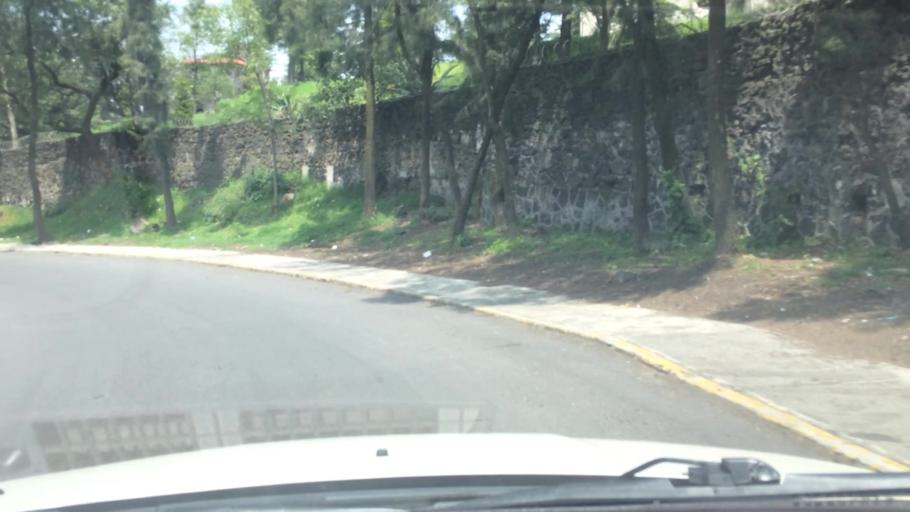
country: MX
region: Mexico City
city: Xochimilco
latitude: 19.2336
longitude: -99.1588
